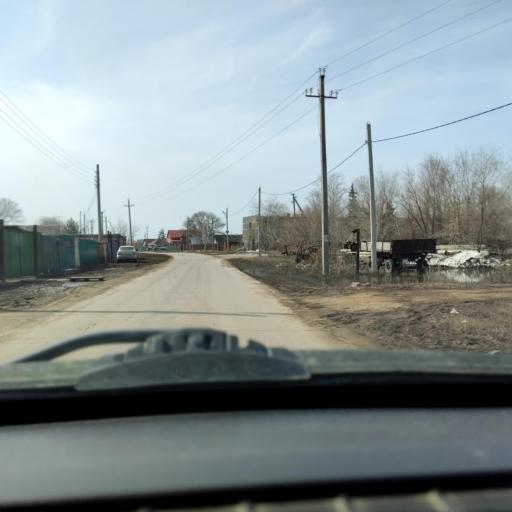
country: RU
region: Samara
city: Smyshlyayevka
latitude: 53.1799
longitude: 50.4448
